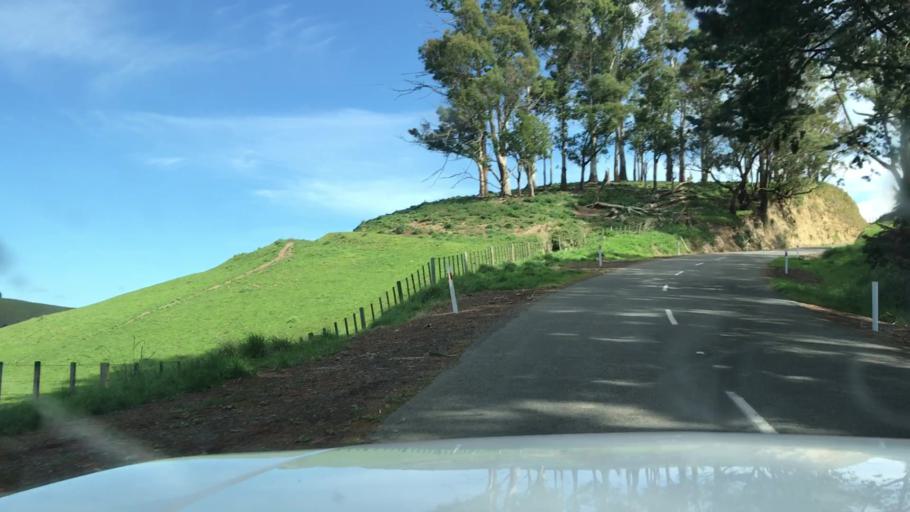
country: NZ
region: Hawke's Bay
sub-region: Hastings District
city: Hastings
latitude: -39.8147
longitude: 176.7516
